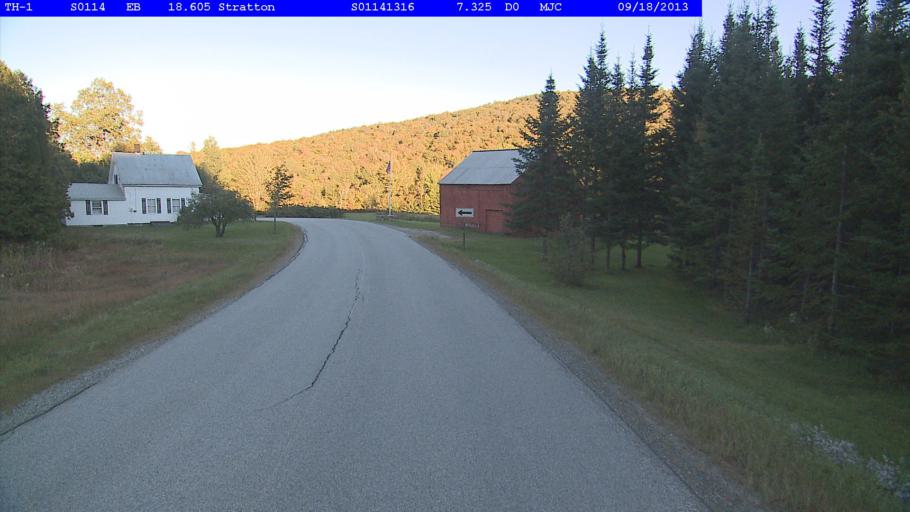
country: US
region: Vermont
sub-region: Windham County
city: Dover
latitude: 43.0259
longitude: -72.8771
